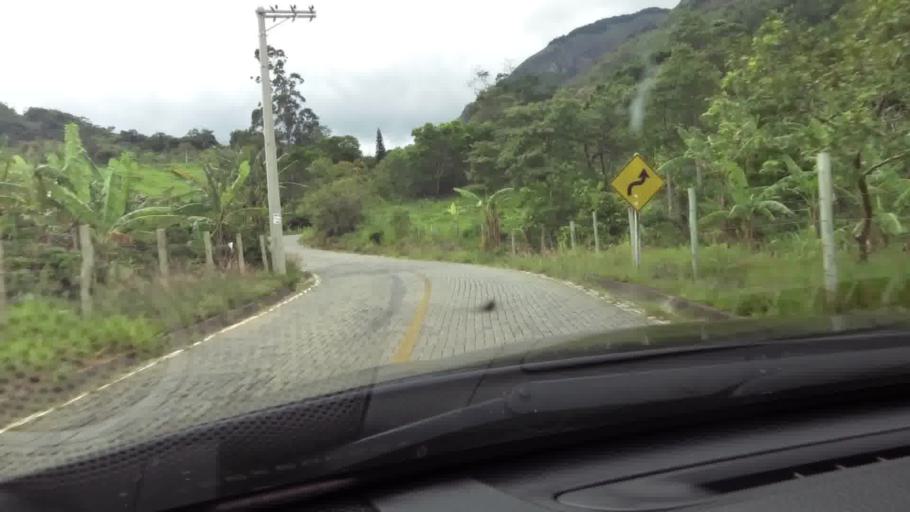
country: BR
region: Espirito Santo
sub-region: Guarapari
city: Guarapari
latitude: -20.6055
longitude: -40.5355
